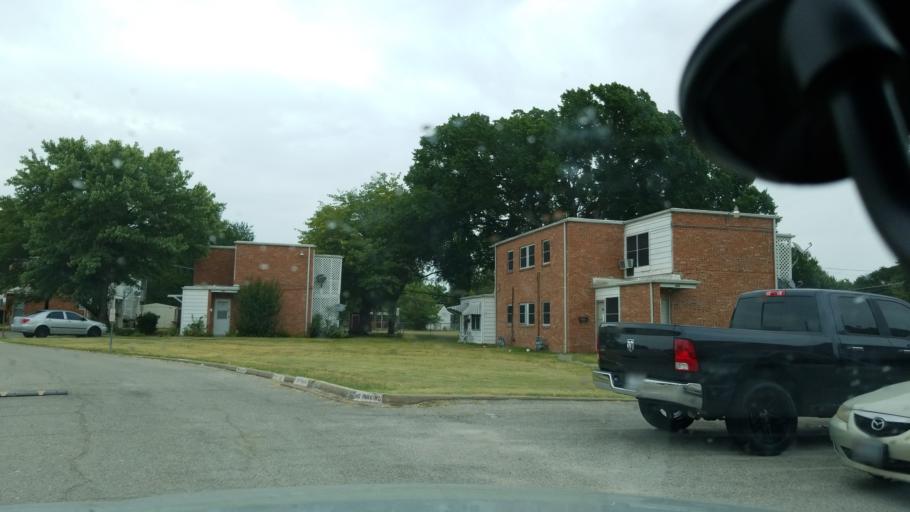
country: US
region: Texas
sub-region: Dallas County
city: Grand Prairie
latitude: 32.7399
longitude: -96.9944
